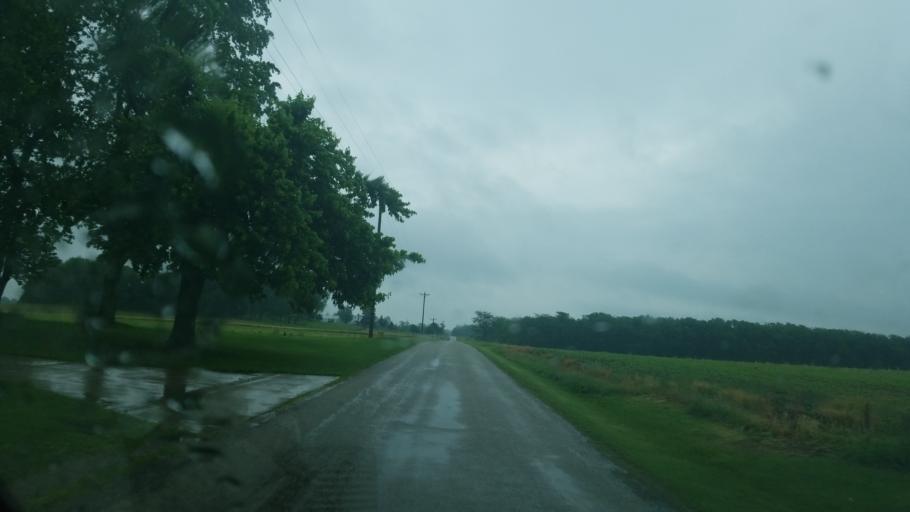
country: US
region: Ohio
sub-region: Huron County
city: Plymouth
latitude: 40.9452
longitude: -82.7358
